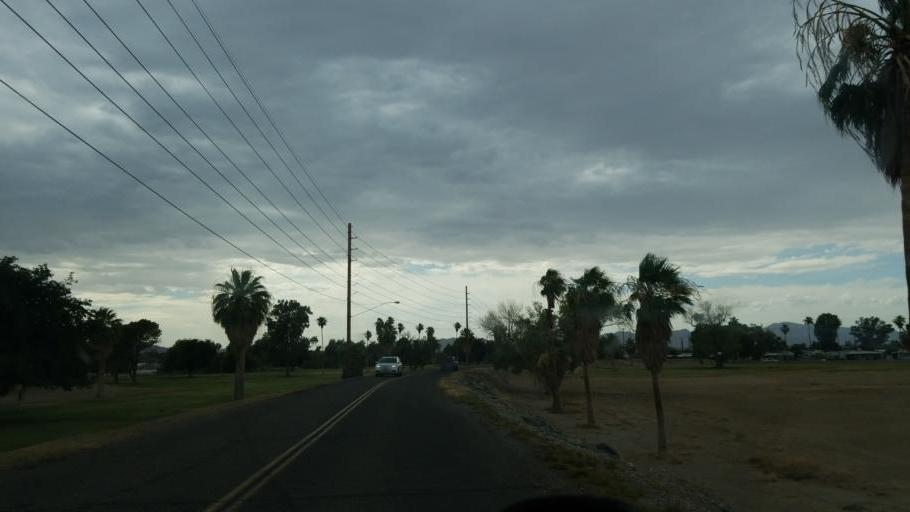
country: US
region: California
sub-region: San Bernardino County
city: Needles
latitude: 34.8446
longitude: -114.6041
